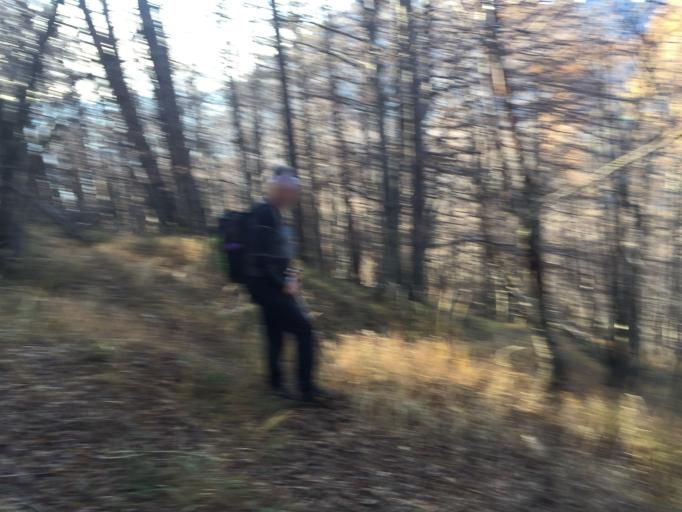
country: IT
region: Friuli Venezia Giulia
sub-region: Provincia di Udine
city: Chiusaforte
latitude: 46.4131
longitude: 13.2811
